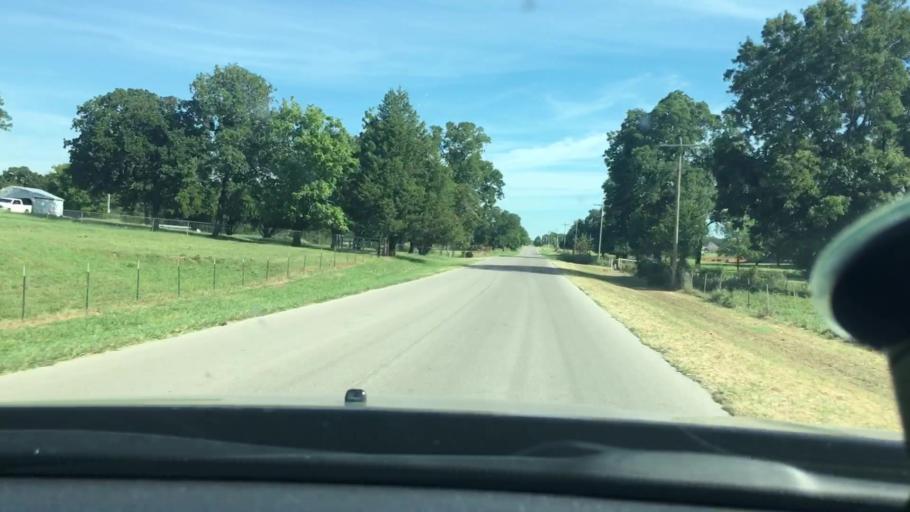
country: US
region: Oklahoma
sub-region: Carter County
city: Lone Grove
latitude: 34.2397
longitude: -97.2474
